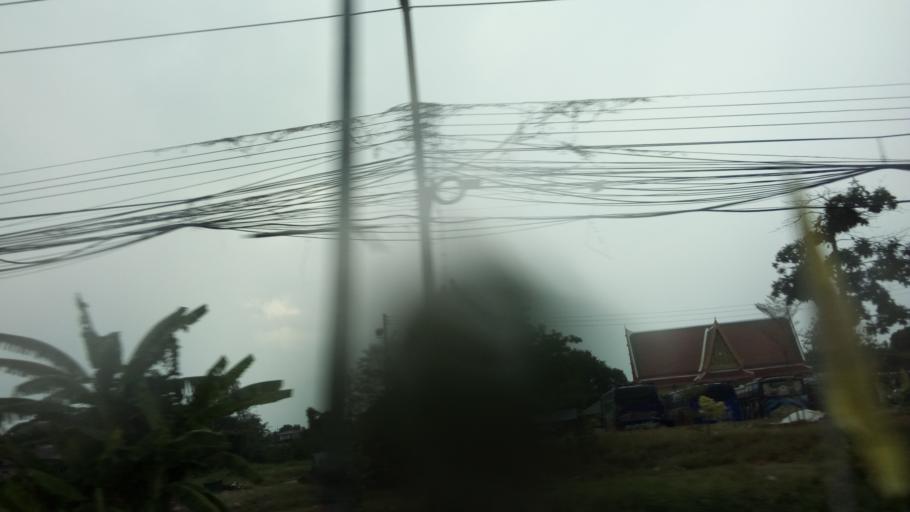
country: TH
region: Phra Nakhon Si Ayutthaya
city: Phra Nakhon Si Ayutthaya
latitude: 14.3505
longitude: 100.5838
